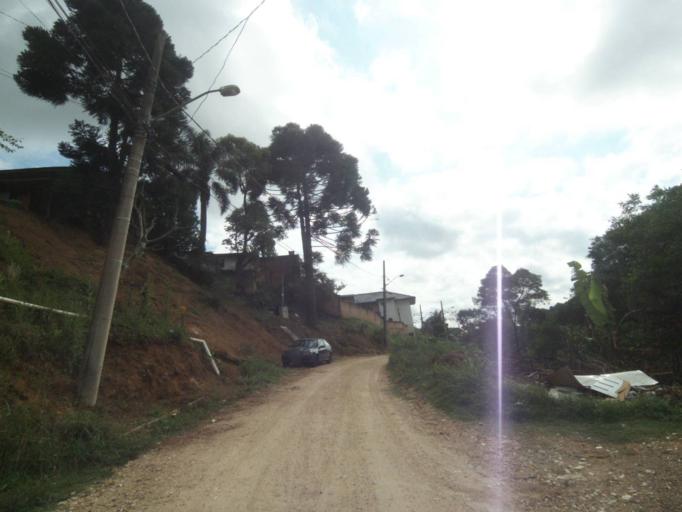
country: BR
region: Parana
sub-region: Curitiba
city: Curitiba
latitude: -25.3789
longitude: -49.2958
